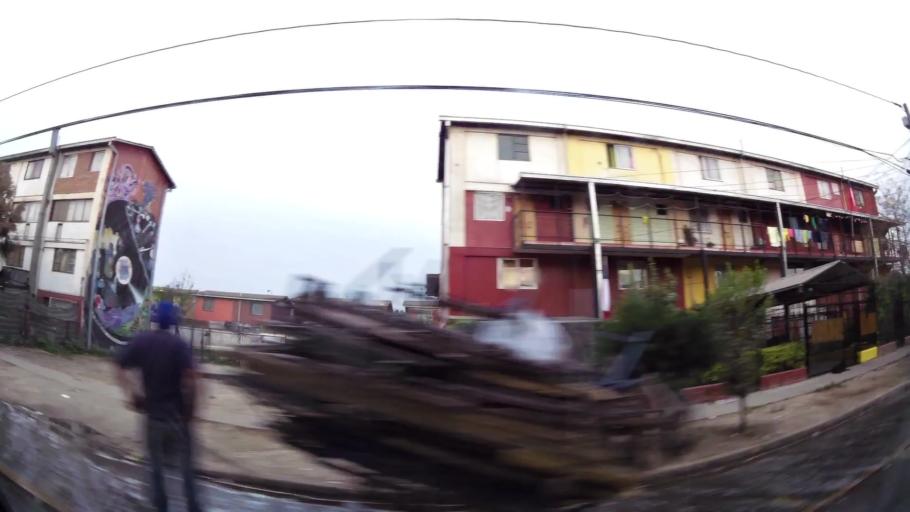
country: CL
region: Santiago Metropolitan
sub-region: Provincia de Santiago
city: Lo Prado
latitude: -33.5171
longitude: -70.7968
